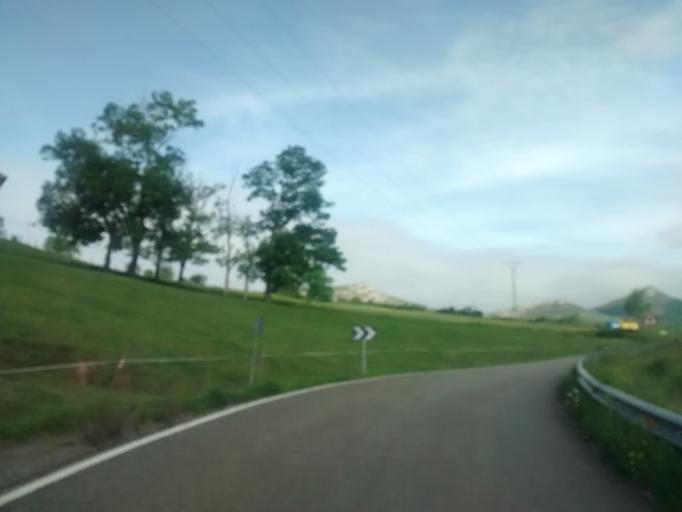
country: ES
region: Cantabria
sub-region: Provincia de Cantabria
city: Potes
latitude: 43.2425
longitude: -4.5622
